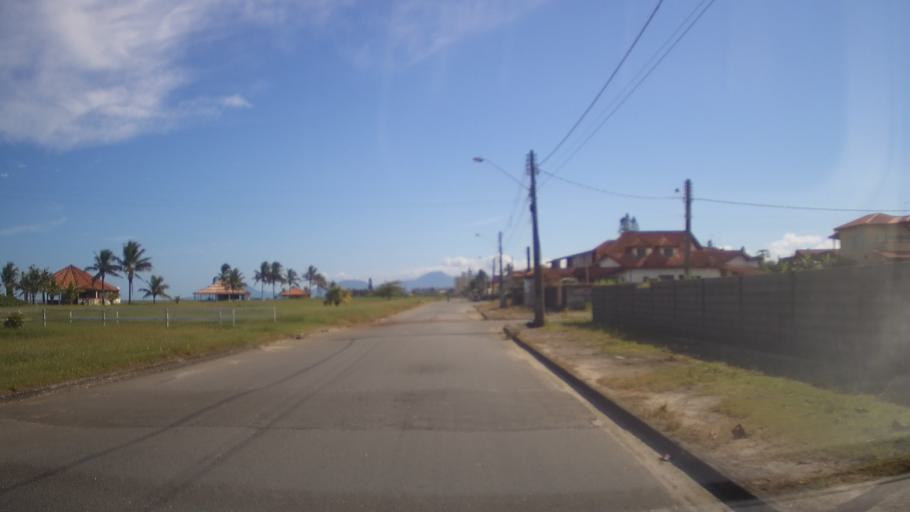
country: BR
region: Sao Paulo
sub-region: Itanhaem
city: Itanhaem
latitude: -24.2095
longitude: -46.8331
